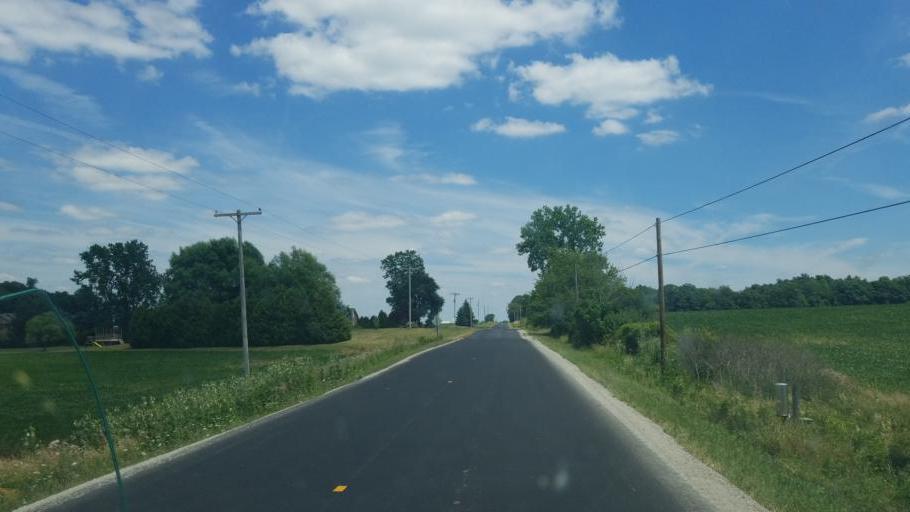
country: US
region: Ohio
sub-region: Williams County
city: Edgerton
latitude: 41.4662
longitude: -84.7077
